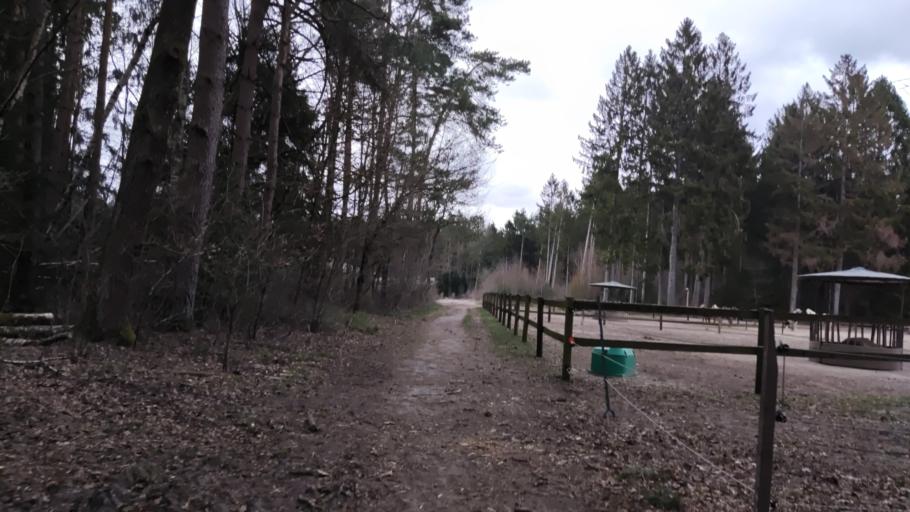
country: DE
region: Lower Saxony
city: Jesteburg
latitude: 53.2874
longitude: 9.9438
